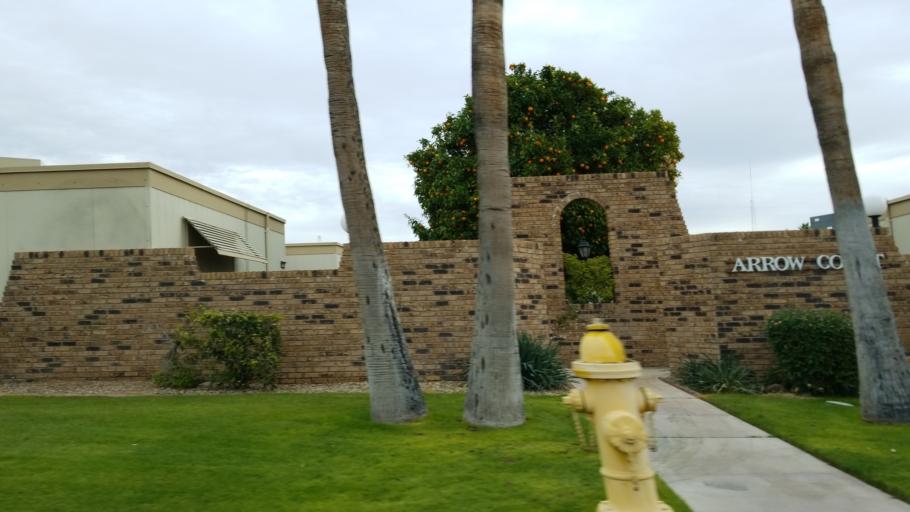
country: US
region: Arizona
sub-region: Maricopa County
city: Youngtown
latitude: 33.6033
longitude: -112.2986
